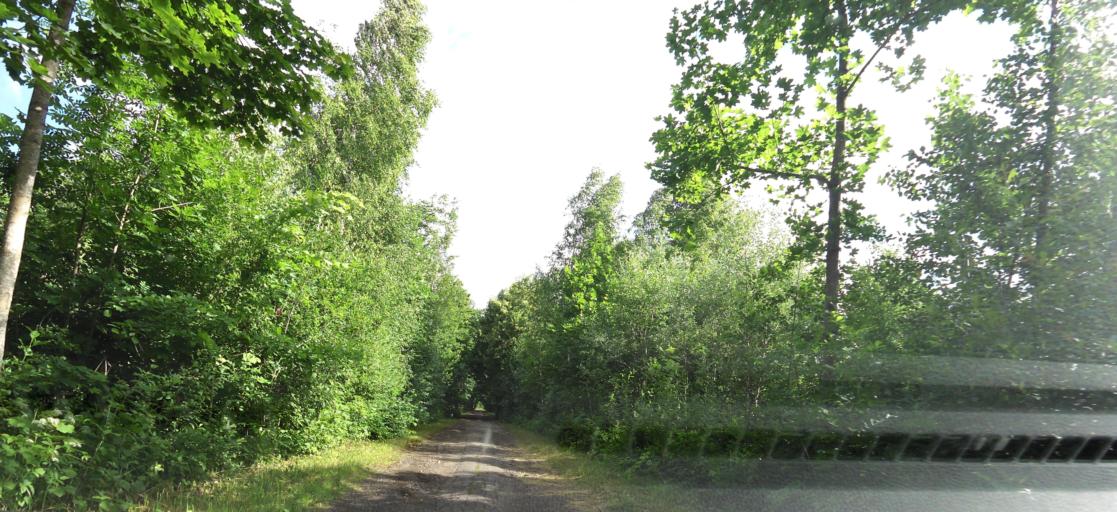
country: LT
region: Panevezys
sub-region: Birzai
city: Birzai
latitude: 56.2214
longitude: 24.7803
